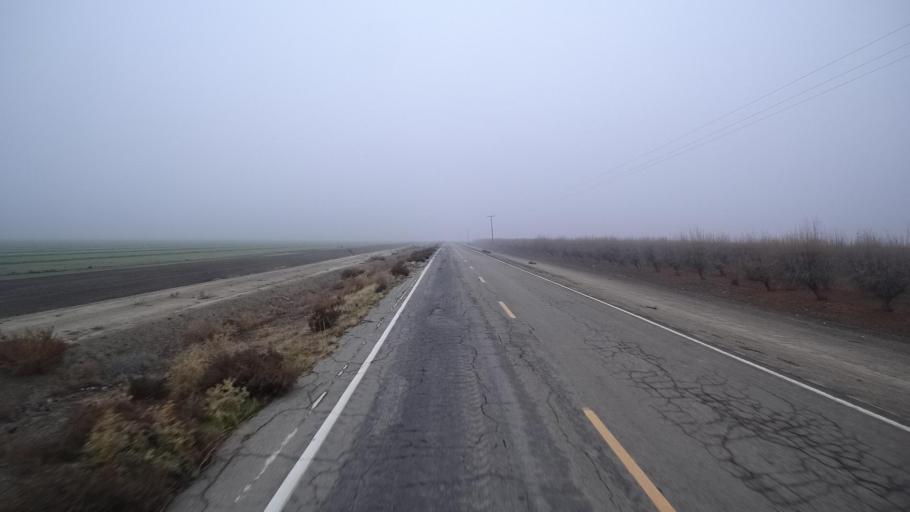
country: US
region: California
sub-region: Kern County
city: Lost Hills
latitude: 35.5708
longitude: -119.6177
